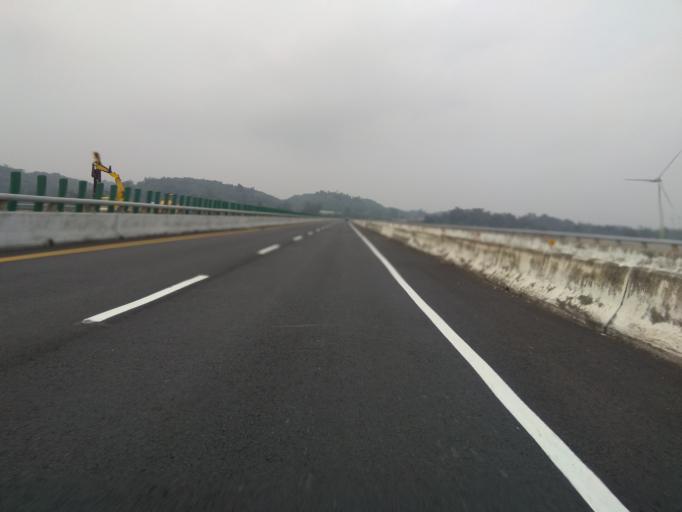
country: TW
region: Taiwan
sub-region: Miaoli
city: Miaoli
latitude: 24.6698
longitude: 120.8353
